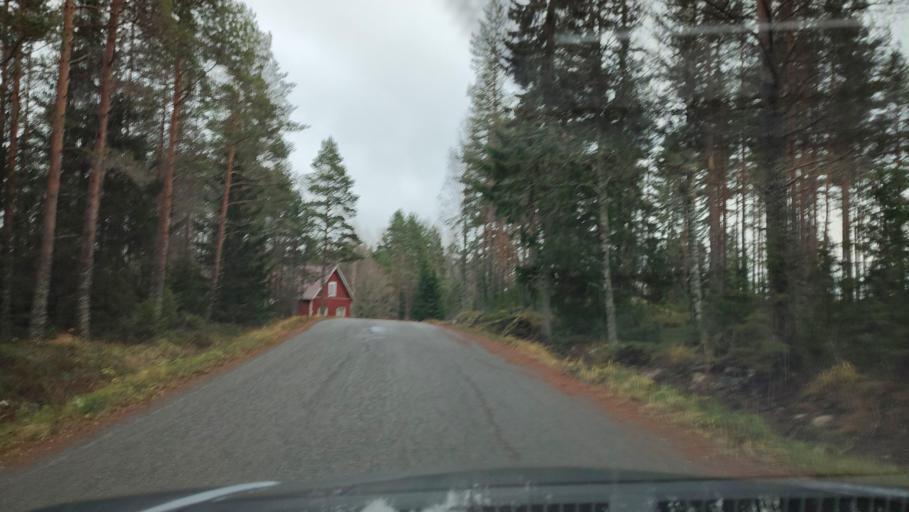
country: FI
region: Southern Ostrobothnia
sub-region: Suupohja
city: Karijoki
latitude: 62.1318
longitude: 21.5765
